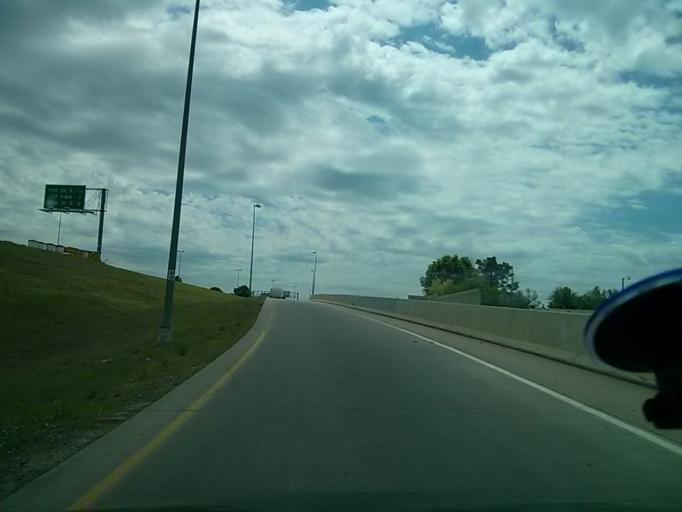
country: US
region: Oklahoma
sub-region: Tulsa County
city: Owasso
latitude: 36.1600
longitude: -95.8616
